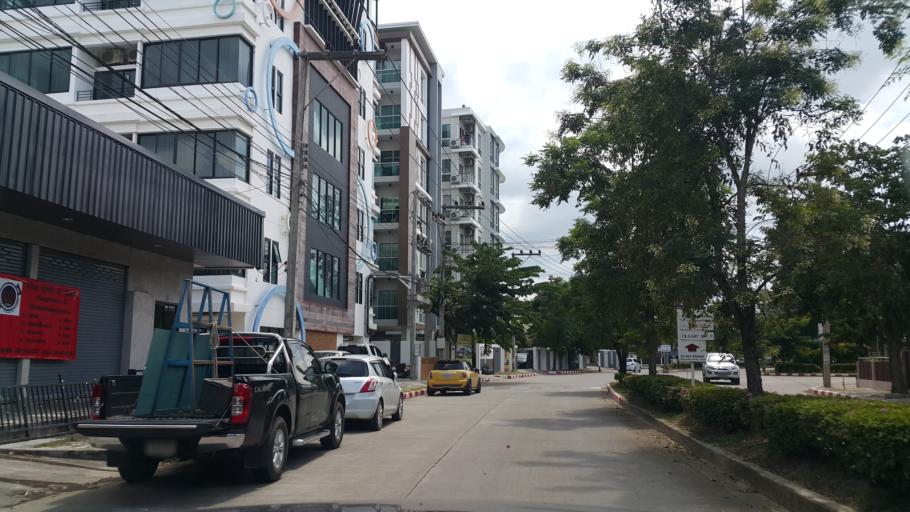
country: TH
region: Chiang Mai
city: Chiang Mai
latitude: 18.8056
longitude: 99.0246
